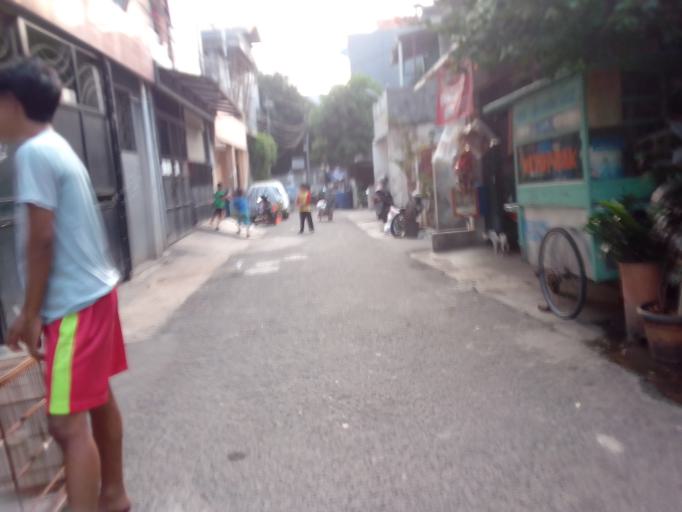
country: ID
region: Jakarta Raya
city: Jakarta
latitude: -6.1938
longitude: 106.8123
